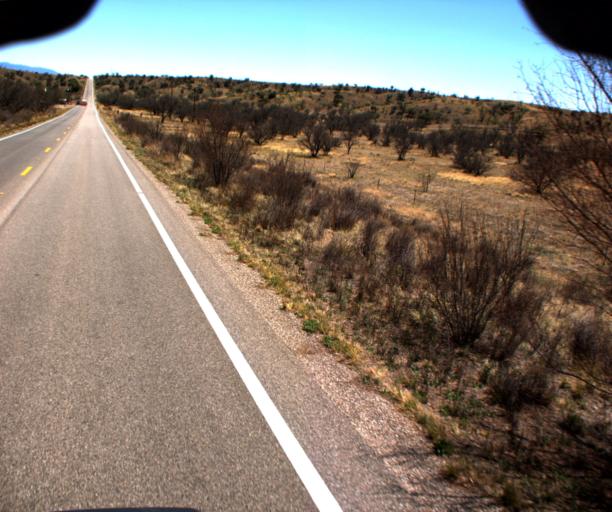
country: US
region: Arizona
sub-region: Pima County
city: Corona de Tucson
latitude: 31.7839
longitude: -110.6949
